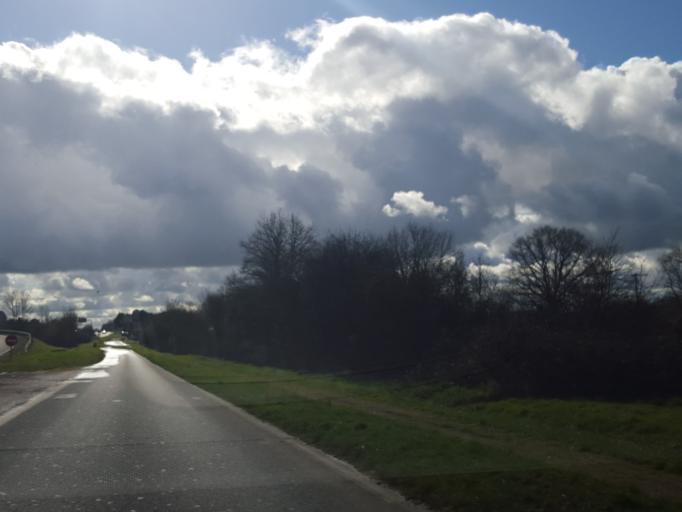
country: FR
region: Pays de la Loire
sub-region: Departement de la Vendee
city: Belleville-sur-Vie
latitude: 46.7728
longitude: -1.4309
